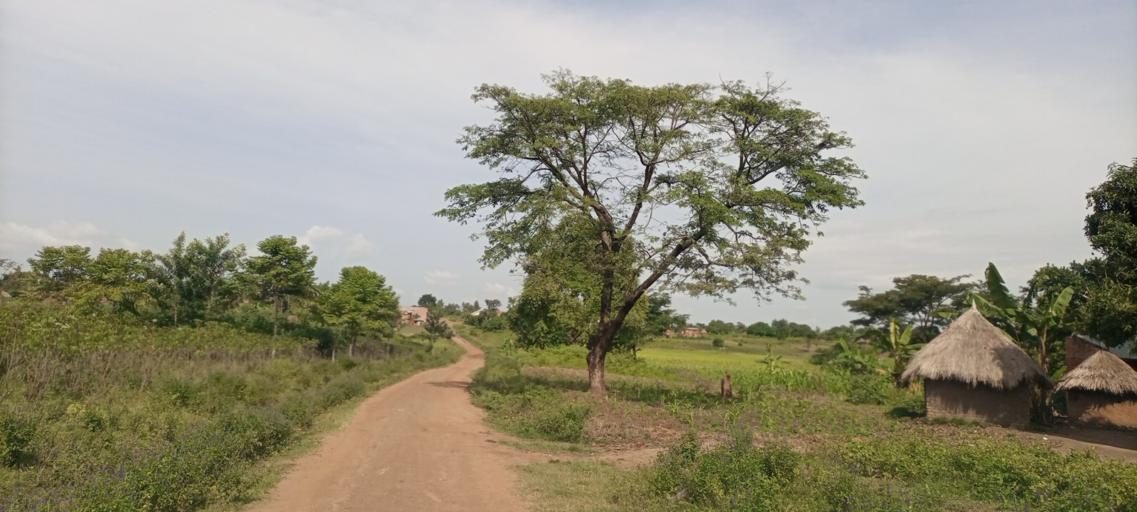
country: UG
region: Eastern Region
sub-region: Mbale District
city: Mbale
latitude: 1.1319
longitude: 34.0481
